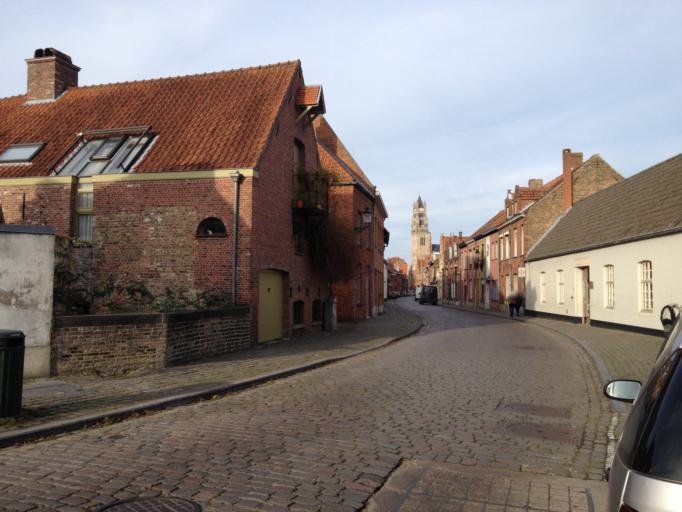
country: BE
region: Flanders
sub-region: Provincie West-Vlaanderen
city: Brugge
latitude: 51.2005
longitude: 3.2208
